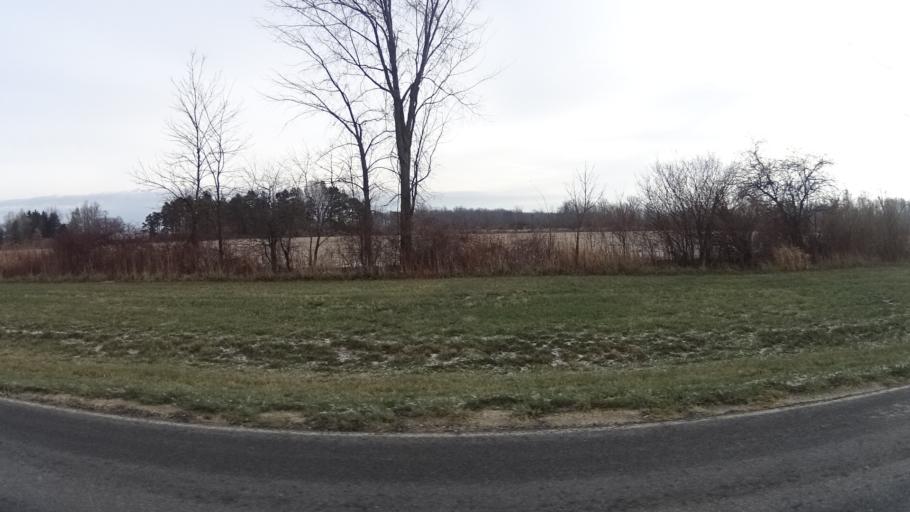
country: US
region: Ohio
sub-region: Lorain County
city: Lagrange
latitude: 41.2344
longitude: -82.1072
